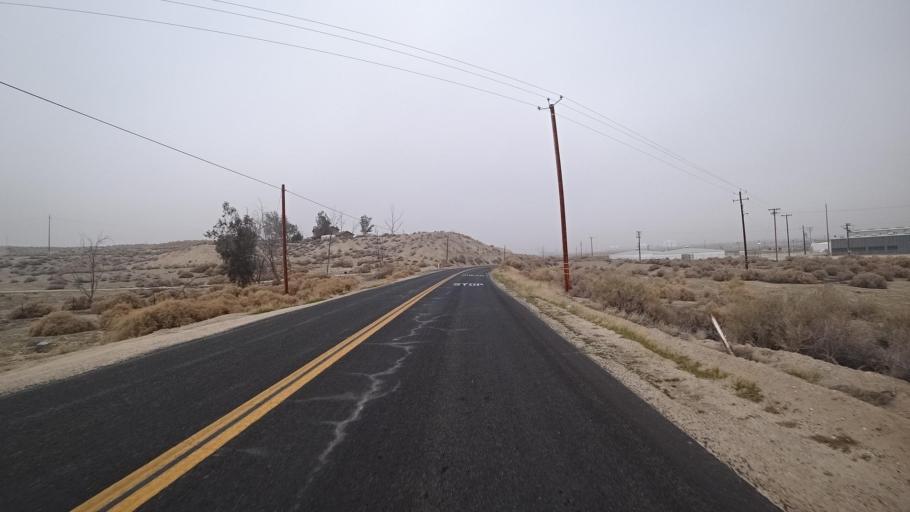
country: US
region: California
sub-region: Kern County
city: Ford City
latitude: 35.2631
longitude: -119.3120
